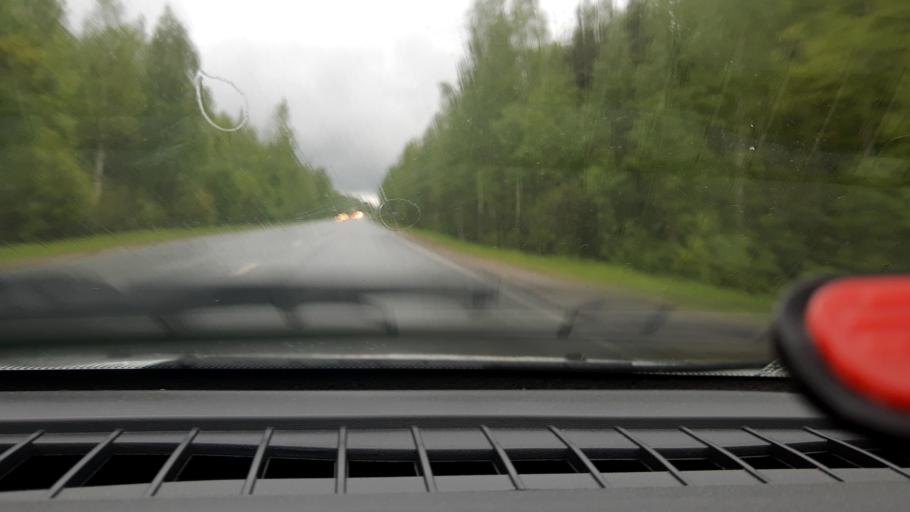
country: RU
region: Nizjnij Novgorod
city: Semenov
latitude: 56.7799
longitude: 44.4321
